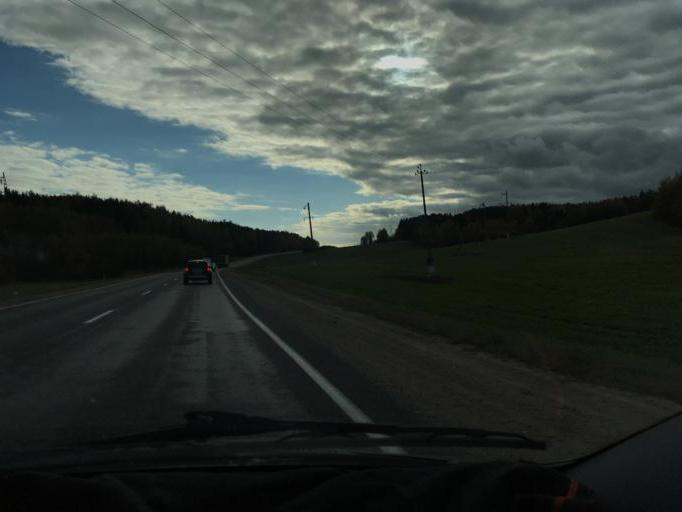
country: BY
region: Minsk
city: Lahoysk
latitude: 54.2201
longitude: 27.8322
